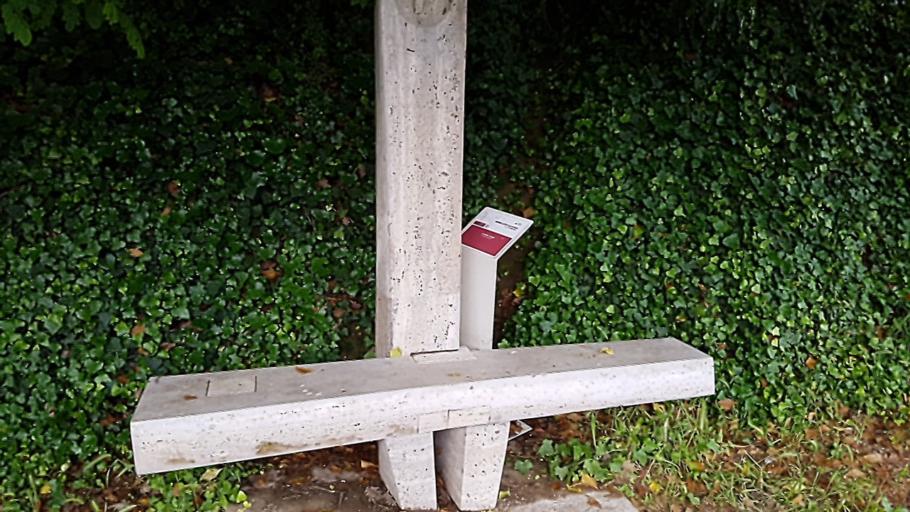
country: IT
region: Tuscany
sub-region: Provincia di Siena
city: Siena
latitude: 43.3237
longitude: 11.3163
